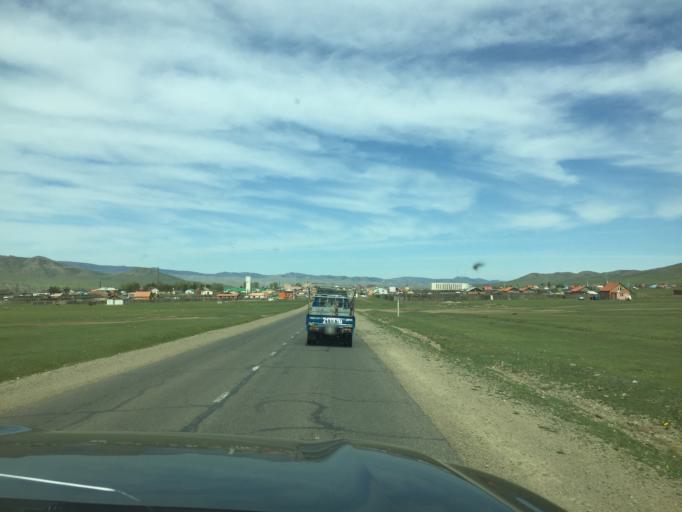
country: MN
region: Central Aimak
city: Ihsueuej
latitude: 48.2189
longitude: 106.3028
